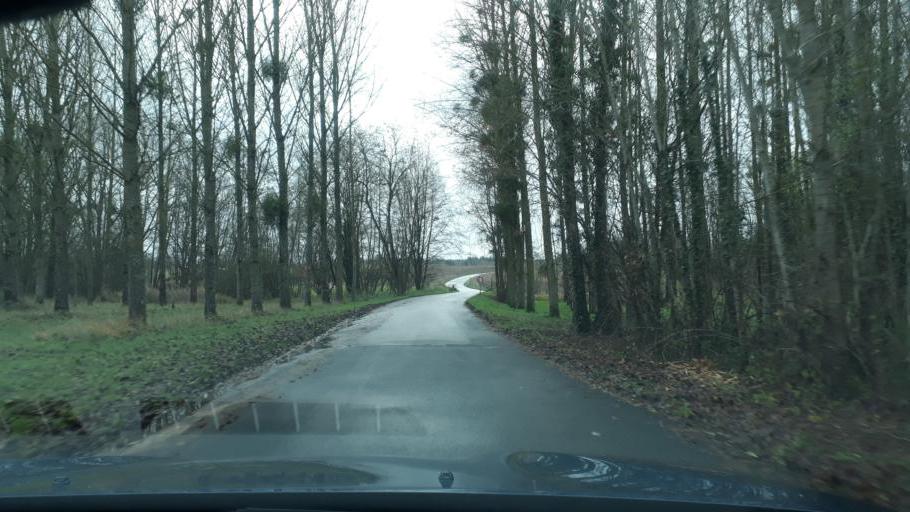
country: FR
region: Centre
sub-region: Departement du Loiret
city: Clery-Saint-Andre
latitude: 47.8200
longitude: 1.7750
